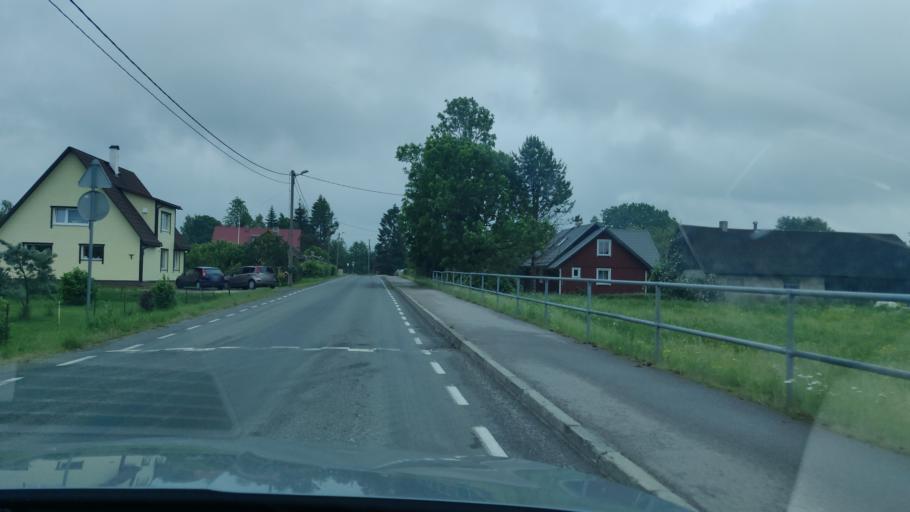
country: EE
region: Jaervamaa
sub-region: Paide linn
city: Paide
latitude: 58.8816
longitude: 25.5824
